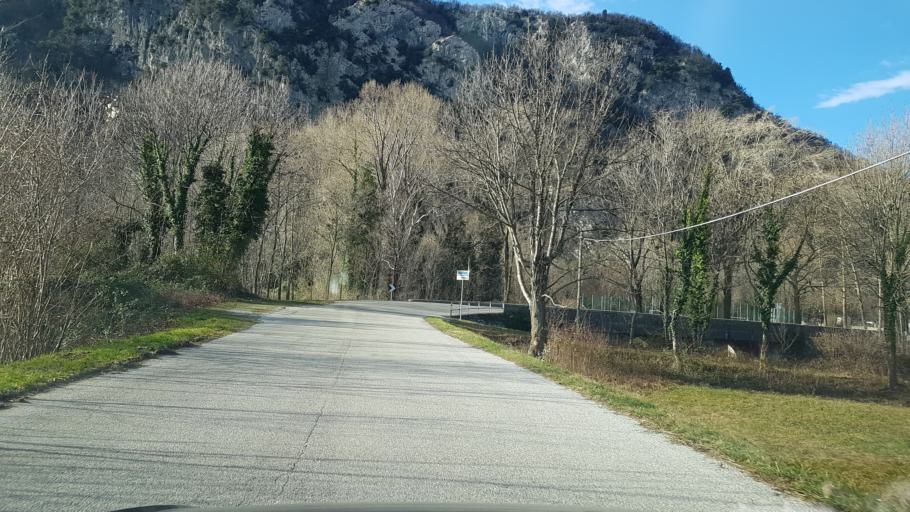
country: IT
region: Friuli Venezia Giulia
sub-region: Provincia di Udine
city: Trasaghis
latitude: 46.2855
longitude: 13.0583
